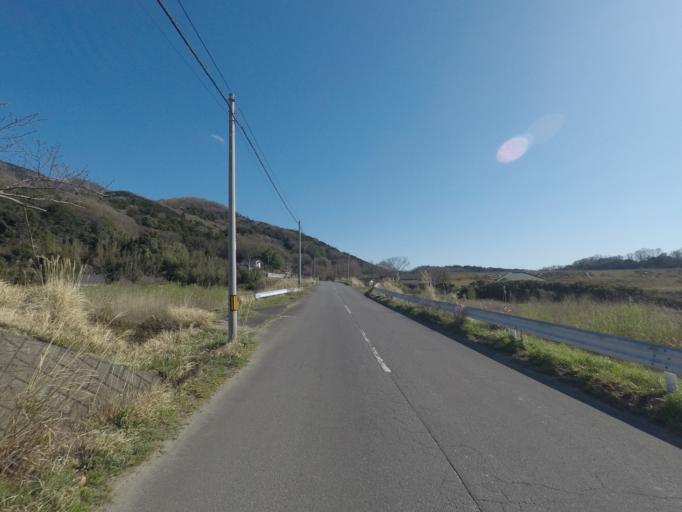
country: JP
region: Ibaraki
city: Makabe
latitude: 36.2430
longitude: 140.0716
